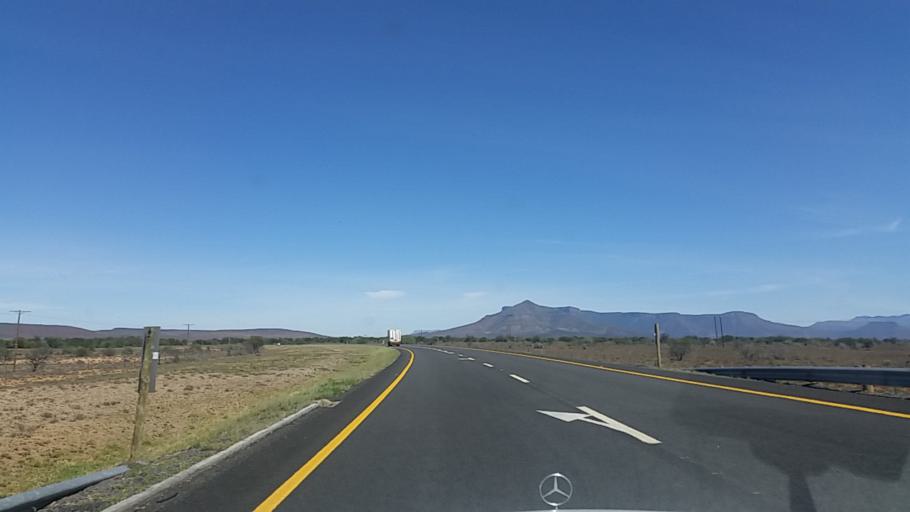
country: ZA
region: Eastern Cape
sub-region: Cacadu District Municipality
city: Graaff-Reinet
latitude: -32.3418
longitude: 24.3744
